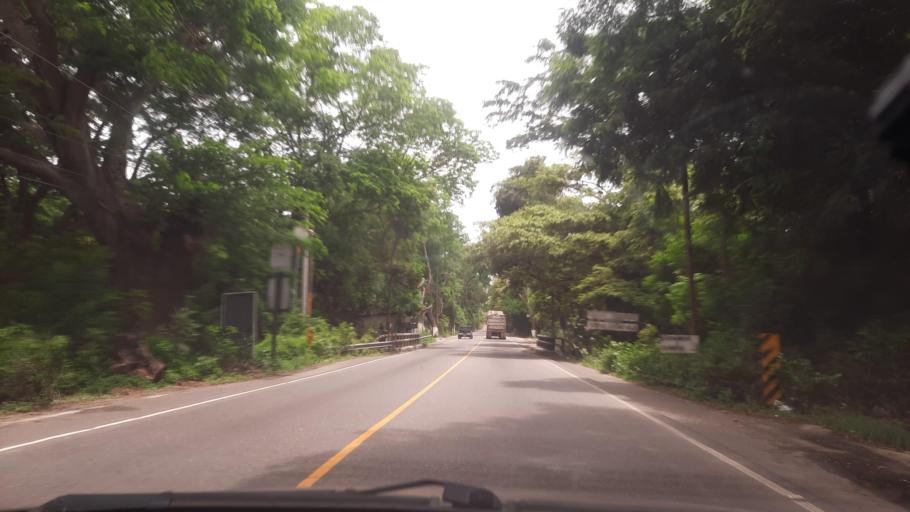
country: GT
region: Zacapa
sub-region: Municipio de Zacapa
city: Gualan
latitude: 15.0898
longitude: -89.4464
